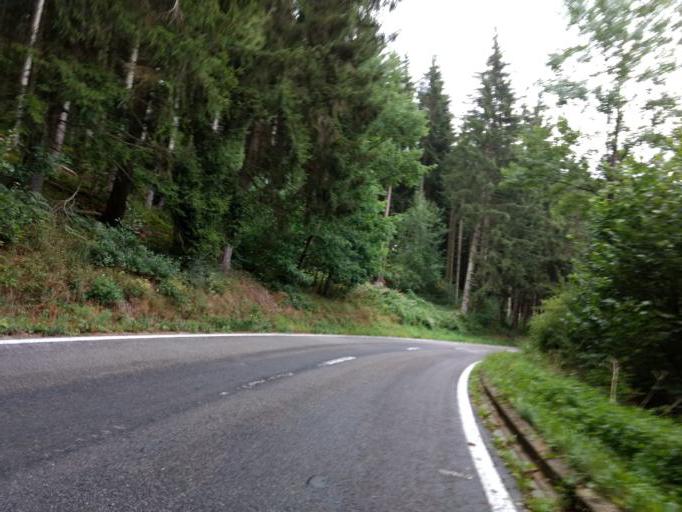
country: BE
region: Wallonia
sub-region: Province du Luxembourg
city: Houffalize
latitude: 50.1352
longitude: 5.7604
